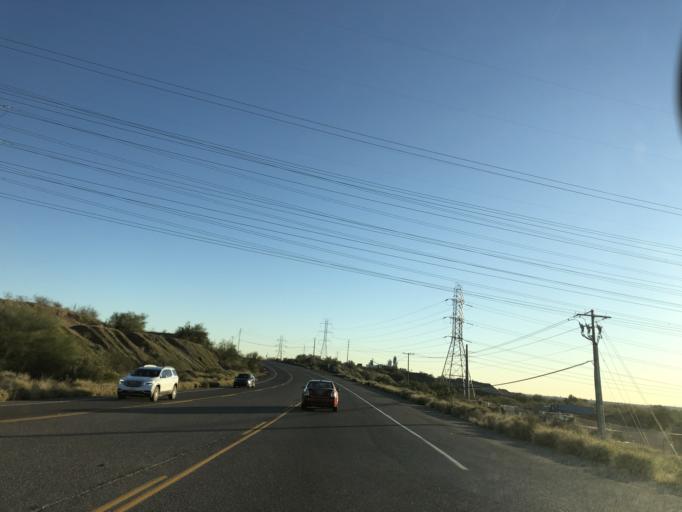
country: US
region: Arizona
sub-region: Maricopa County
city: Sun City West
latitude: 33.7071
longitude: -112.2895
